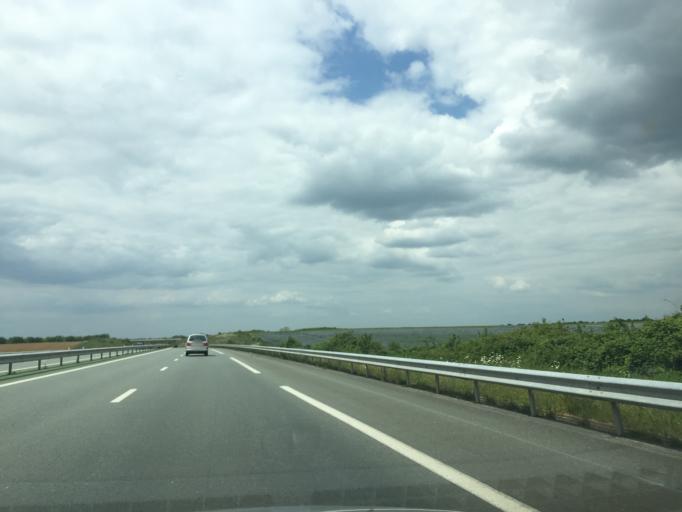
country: FR
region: Poitou-Charentes
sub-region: Departement des Deux-Sevres
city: Echire
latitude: 46.4173
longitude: -0.4038
